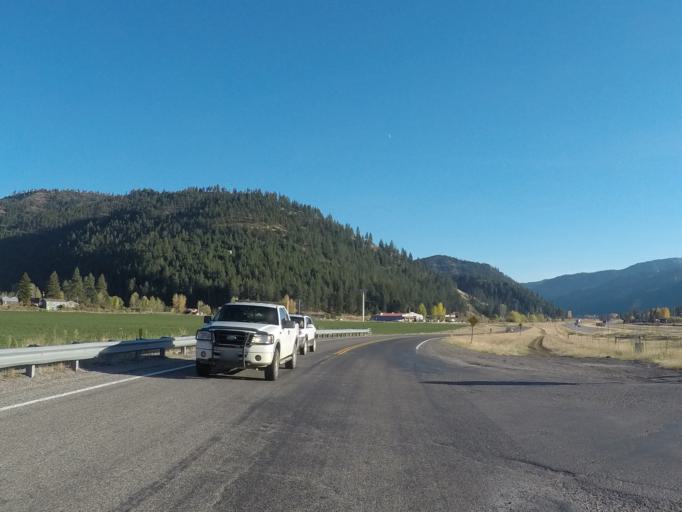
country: US
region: Montana
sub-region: Missoula County
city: Clinton
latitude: 46.7813
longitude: -113.7122
